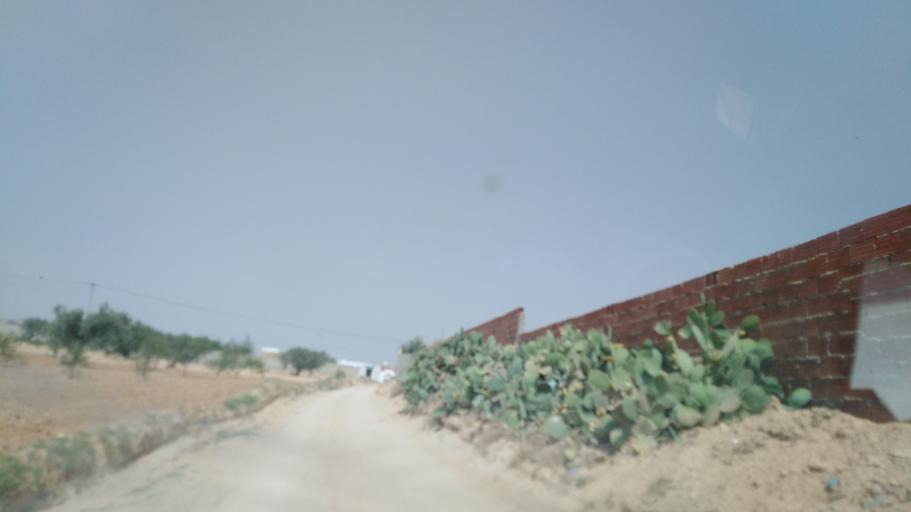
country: TN
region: Safaqis
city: Sfax
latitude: 34.6251
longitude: 10.5758
